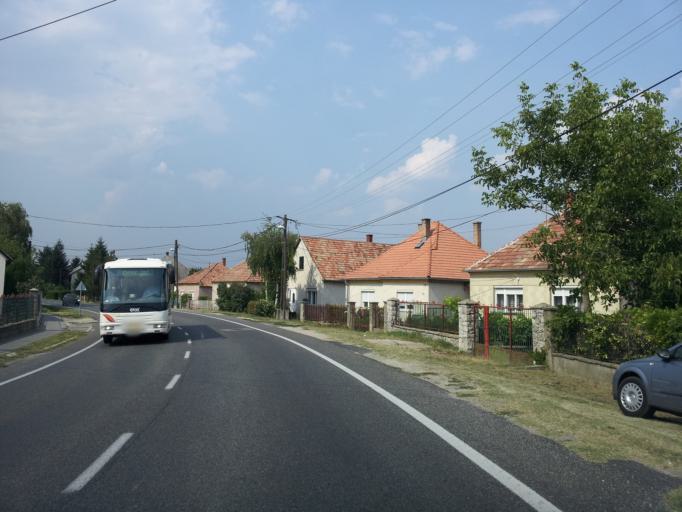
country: HU
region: Gyor-Moson-Sopron
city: Nyul
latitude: 47.5800
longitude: 17.6974
